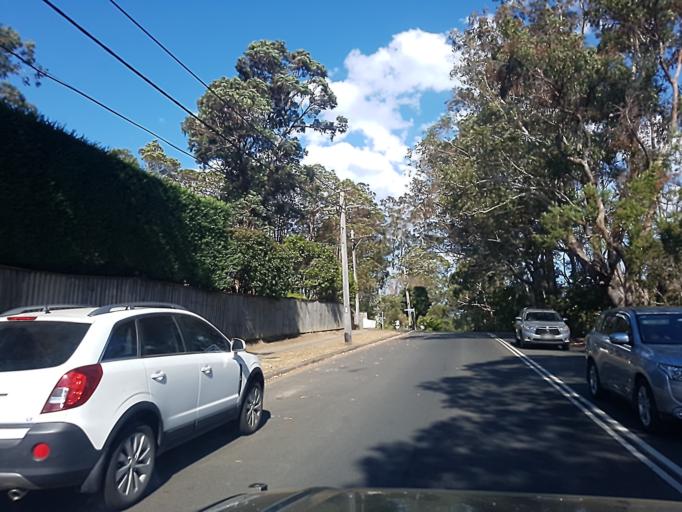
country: AU
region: New South Wales
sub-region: Ku-ring-gai
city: North Wahroonga
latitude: -33.7129
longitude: 151.1101
